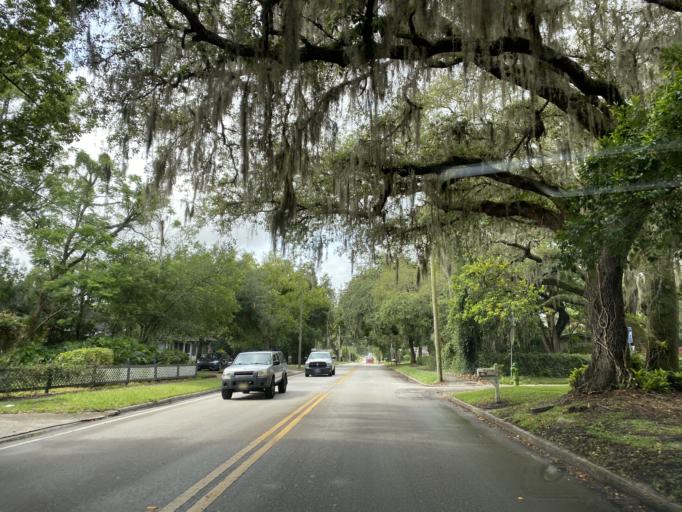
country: US
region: Florida
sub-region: Seminole County
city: Sanford
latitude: 28.7924
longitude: -81.2649
